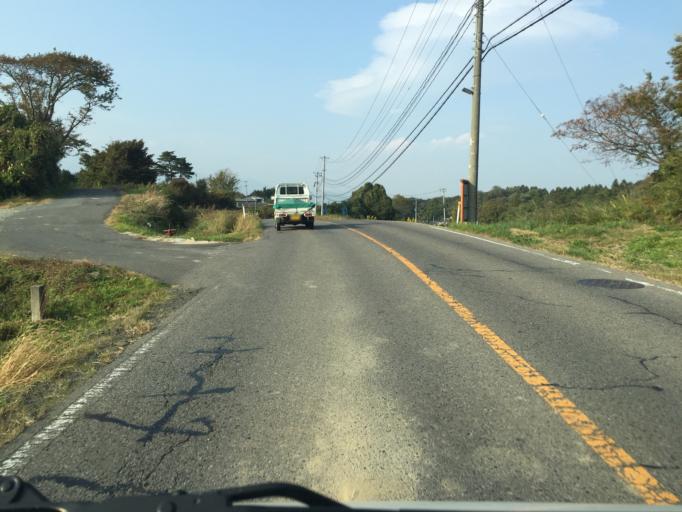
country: JP
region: Fukushima
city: Motomiya
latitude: 37.4674
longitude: 140.3902
